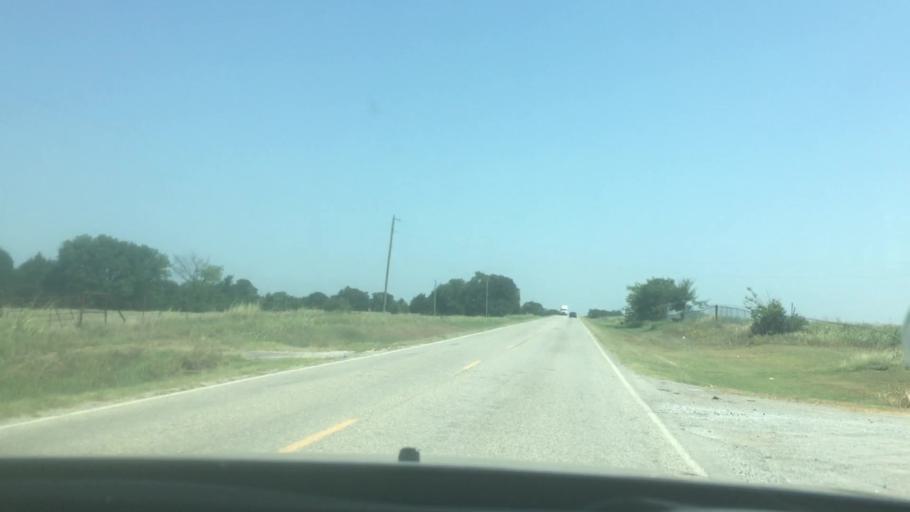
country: US
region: Oklahoma
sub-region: Johnston County
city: Tishomingo
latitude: 34.3096
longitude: -96.4247
